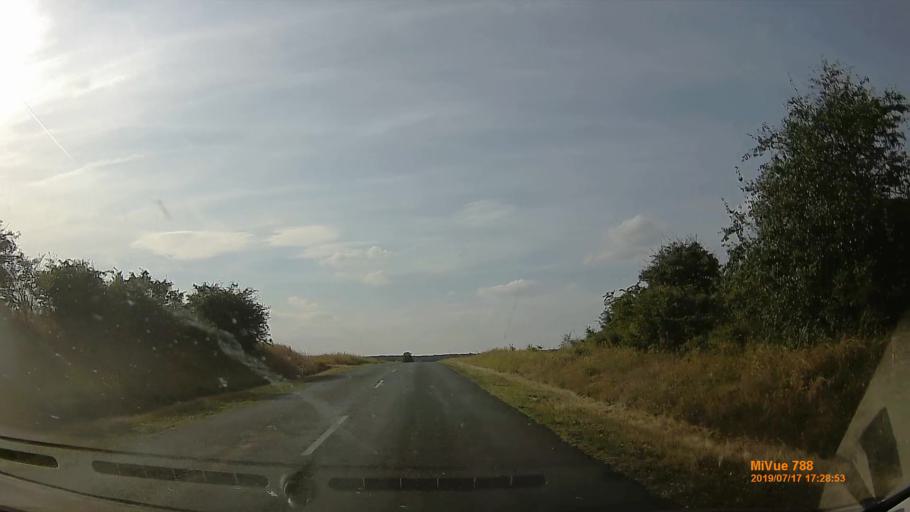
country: HU
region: Veszprem
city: Urkut
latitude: 47.0113
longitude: 17.5909
